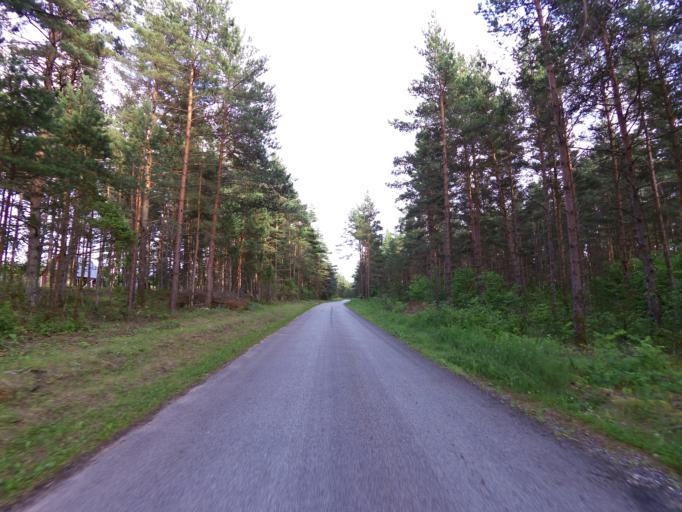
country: EE
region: Laeaene
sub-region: Vormsi vald
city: Hullo
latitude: 58.9786
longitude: 23.2547
